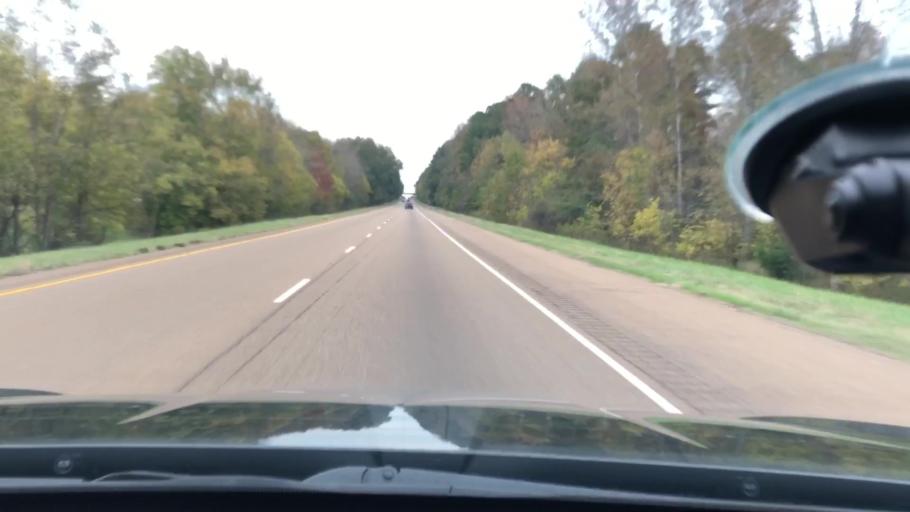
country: US
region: Arkansas
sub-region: Nevada County
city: Prescott
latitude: 33.7712
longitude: -93.4768
